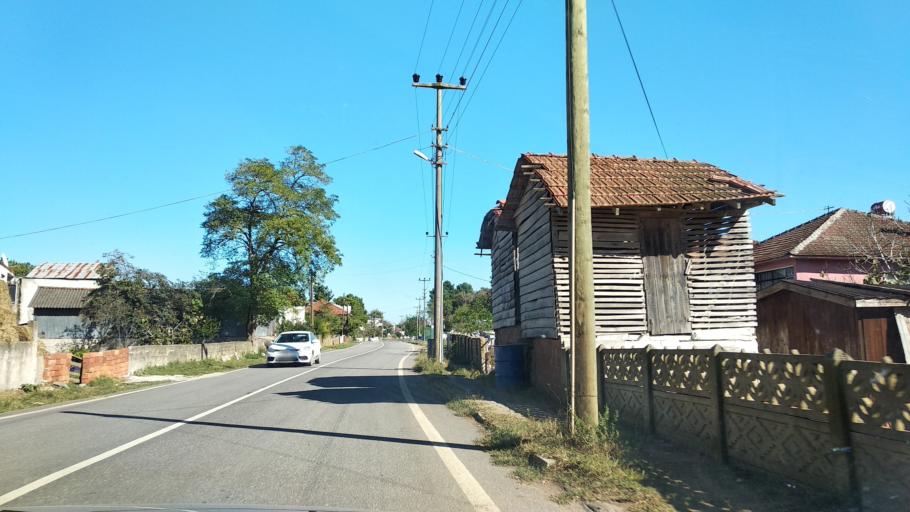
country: TR
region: Sakarya
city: Karasu
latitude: 41.1182
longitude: 30.6275
